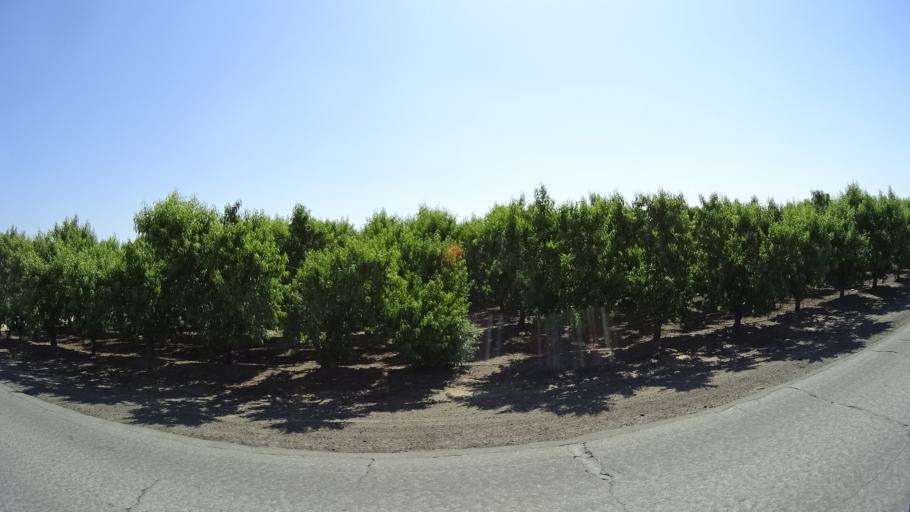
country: US
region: California
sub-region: Fresno County
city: Kingsburg
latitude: 36.4287
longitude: -119.5287
